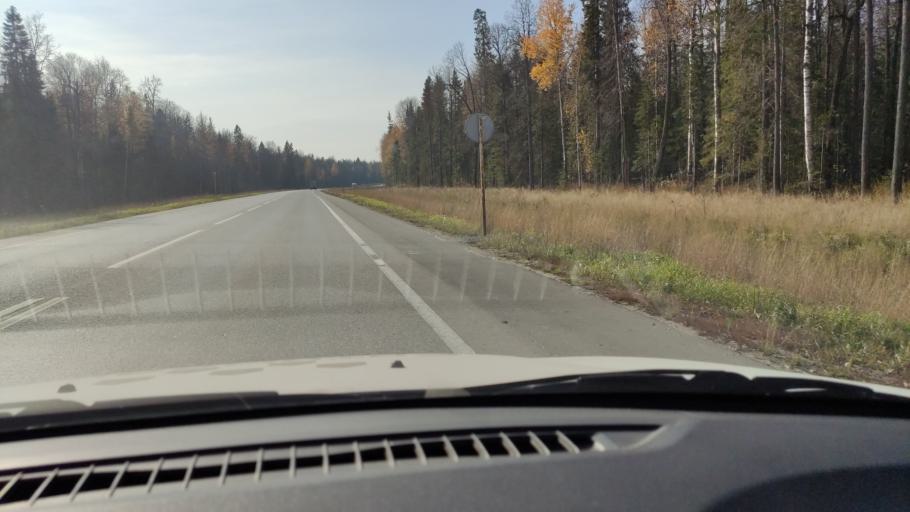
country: RU
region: Perm
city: Novyye Lyady
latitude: 58.0345
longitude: 56.5322
